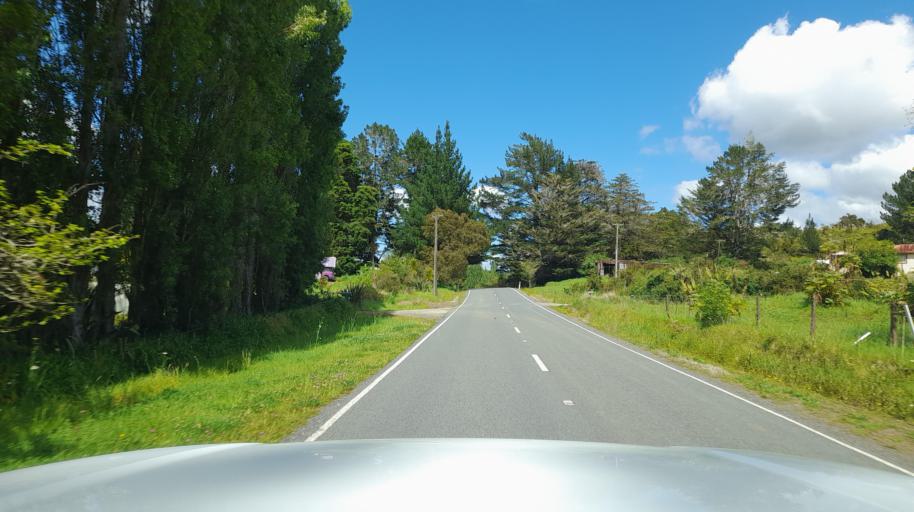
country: NZ
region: Northland
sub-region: Far North District
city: Taipa
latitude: -35.0889
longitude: 173.5048
